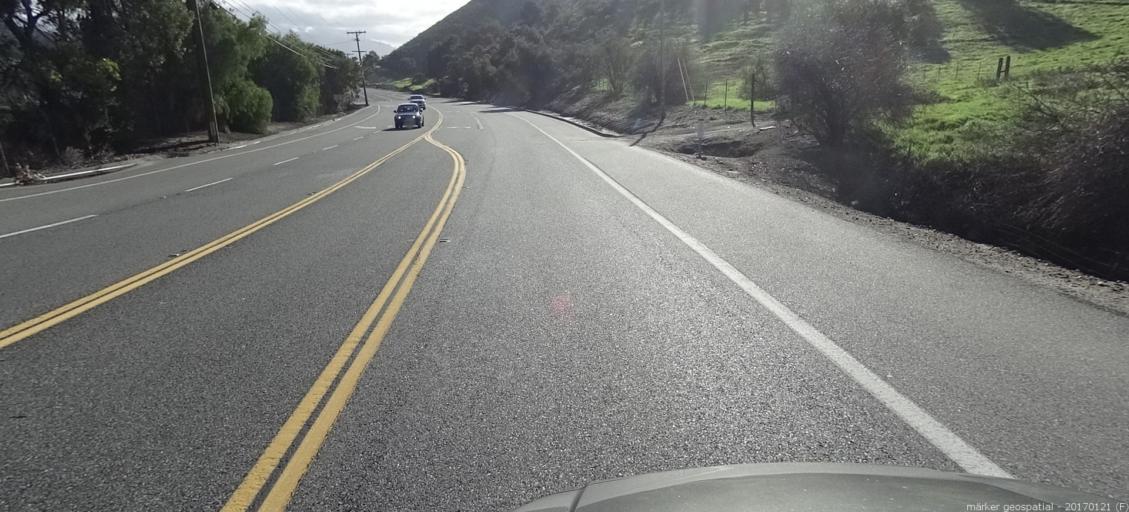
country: US
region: California
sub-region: Orange County
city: North Tustin
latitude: 33.7636
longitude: -117.7130
